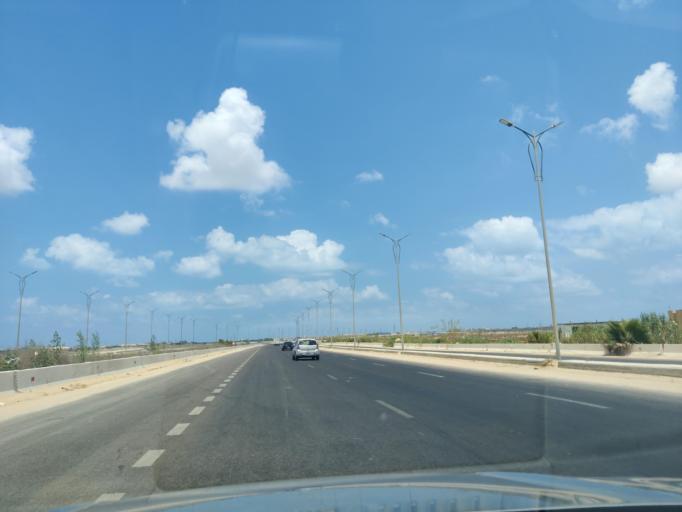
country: EG
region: Alexandria
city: Alexandria
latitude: 30.9891
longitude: 29.6533
